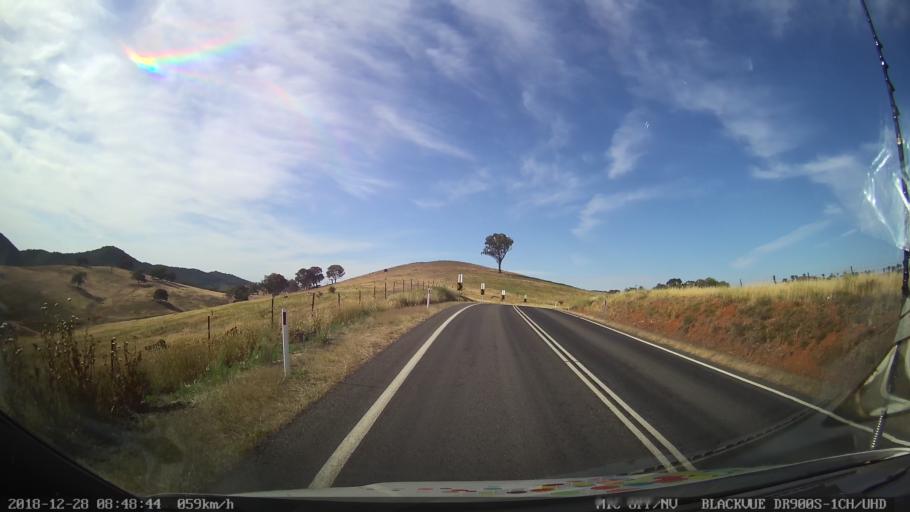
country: AU
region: New South Wales
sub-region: Upper Lachlan Shire
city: Crookwell
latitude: -34.0397
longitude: 149.3365
